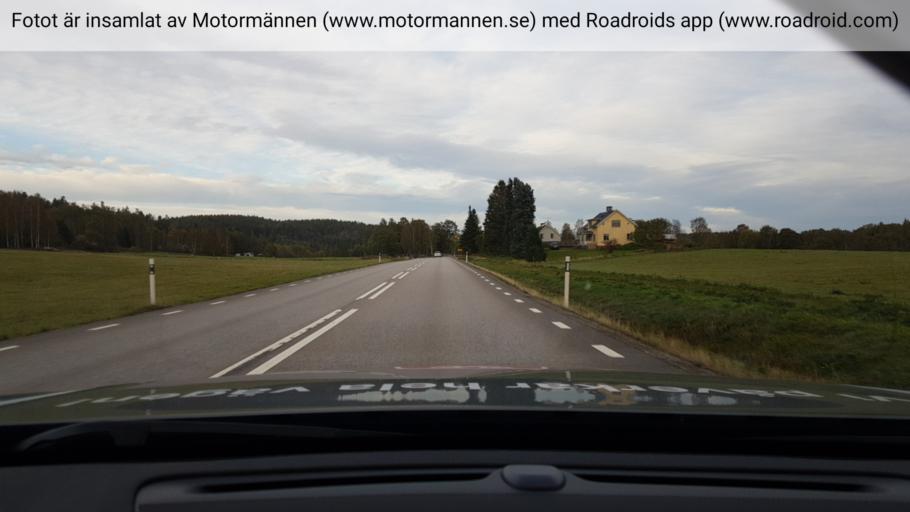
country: SE
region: Vaestra Goetaland
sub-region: Bengtsfors Kommun
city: Billingsfors
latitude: 59.0303
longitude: 12.3055
